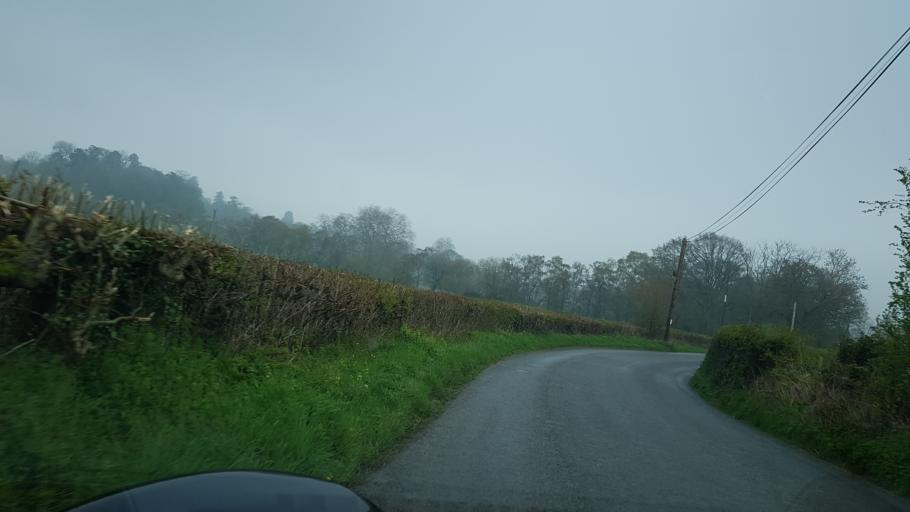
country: GB
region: England
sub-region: Herefordshire
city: Brockhampton
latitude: 52.0118
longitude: -2.5776
